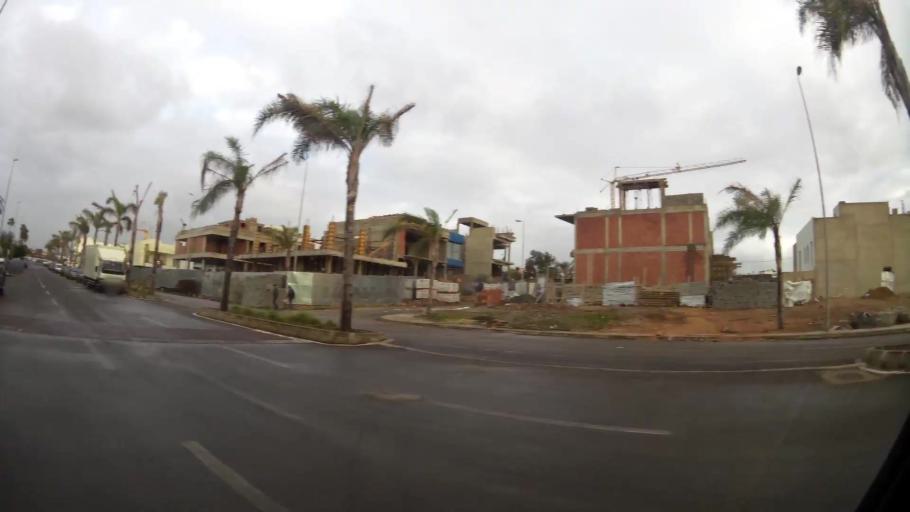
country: MA
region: Grand Casablanca
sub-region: Casablanca
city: Casablanca
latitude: 33.5827
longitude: -7.6796
